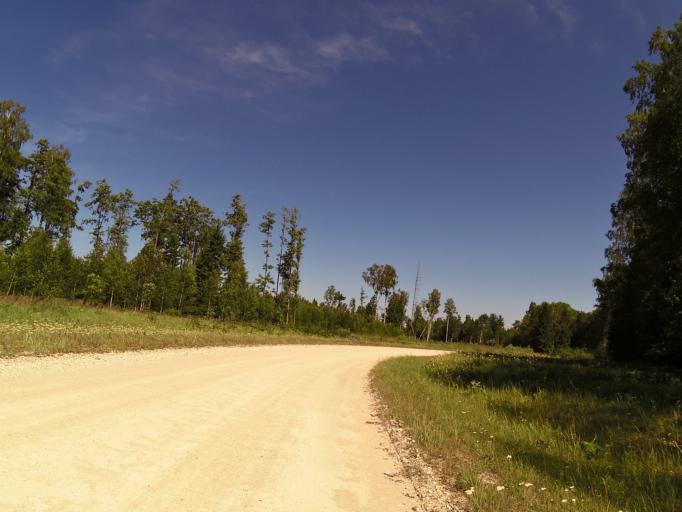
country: EE
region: Hiiumaa
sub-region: Kaerdla linn
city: Kardla
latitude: 58.9261
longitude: 22.3680
